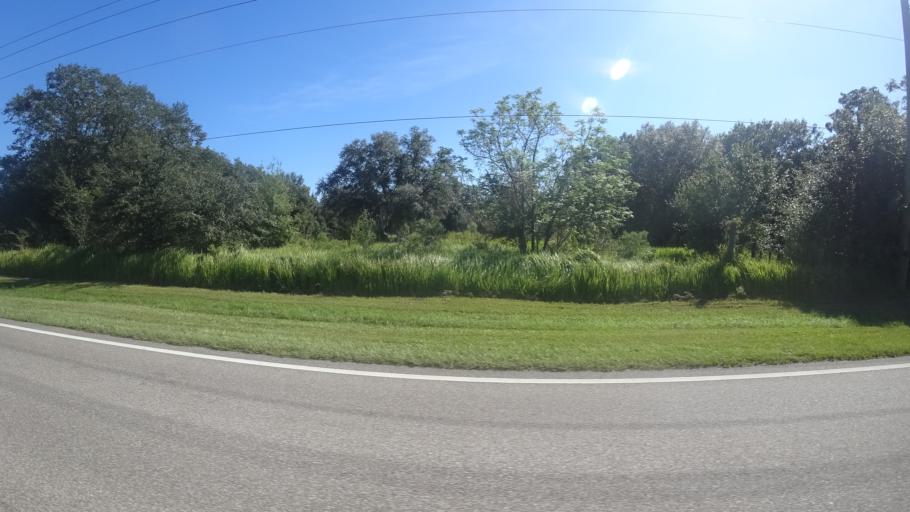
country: US
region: Florida
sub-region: Sarasota County
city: Lake Sarasota
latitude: 27.3523
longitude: -82.2686
